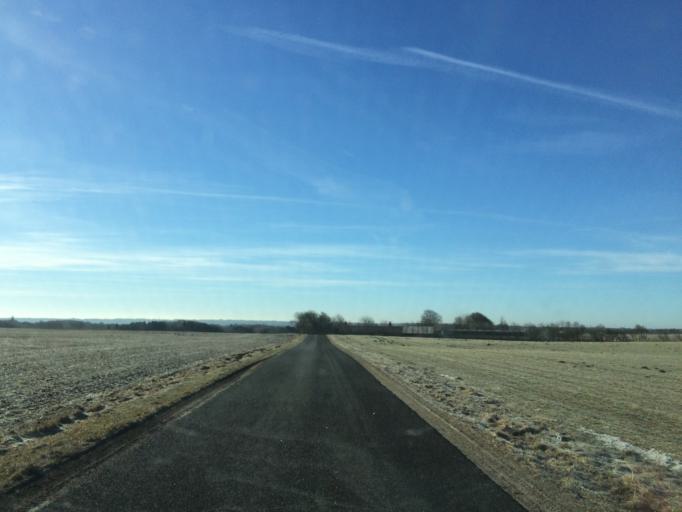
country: DK
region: North Denmark
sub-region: Mariagerfjord Kommune
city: Hobro
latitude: 56.6304
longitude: 9.6452
